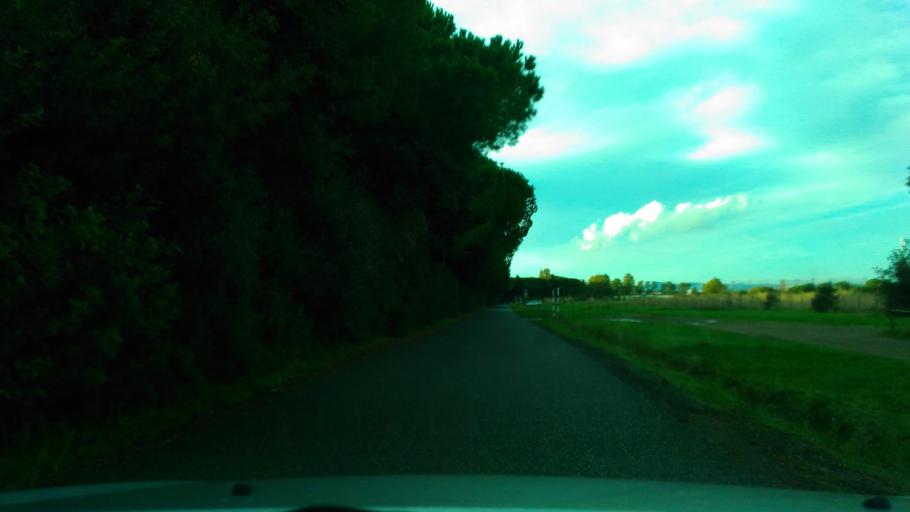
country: IT
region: Tuscany
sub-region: Provincia di Livorno
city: Cecina
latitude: 43.2885
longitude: 10.5087
